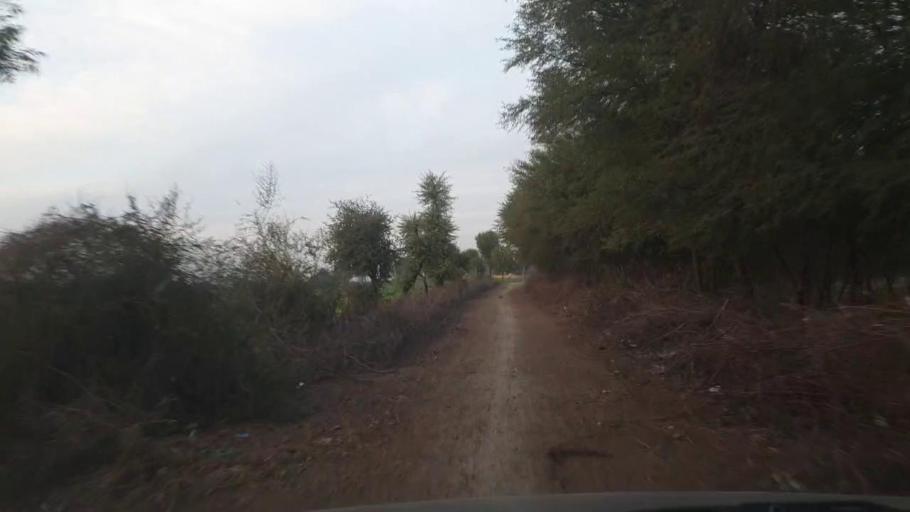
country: PK
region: Sindh
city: Shahpur Chakar
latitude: 26.0705
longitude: 68.5359
